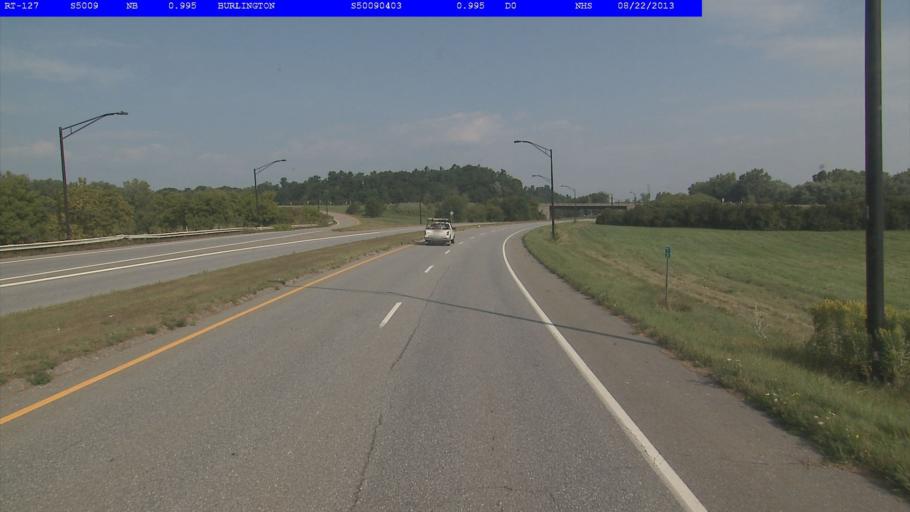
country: US
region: Vermont
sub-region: Chittenden County
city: Burlington
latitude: 44.4996
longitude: -73.2297
